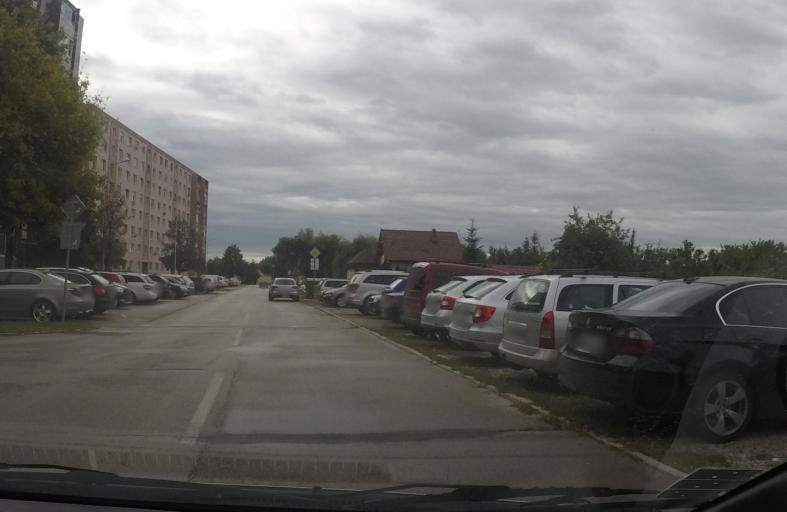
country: SK
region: Trnavsky
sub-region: Okres Galanta
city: Galanta
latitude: 48.1920
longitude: 17.7132
